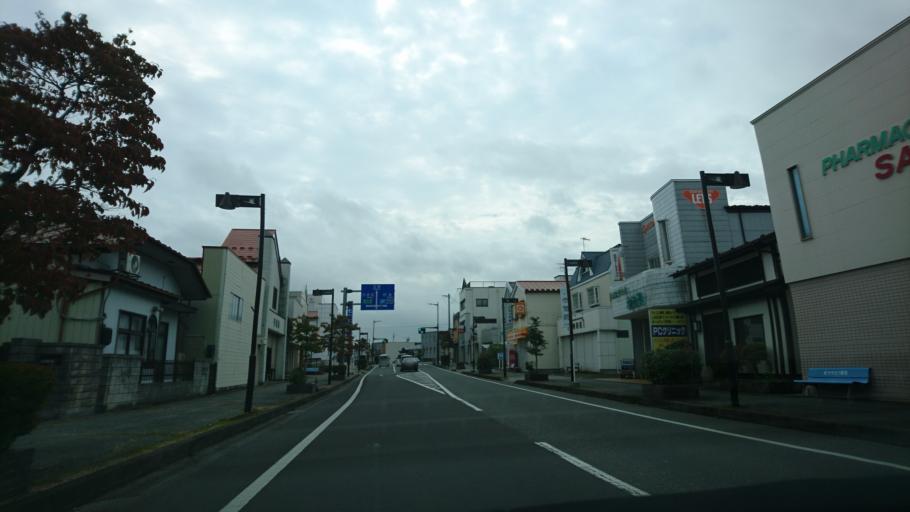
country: JP
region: Iwate
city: Ichinoseki
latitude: 38.7729
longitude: 141.1296
